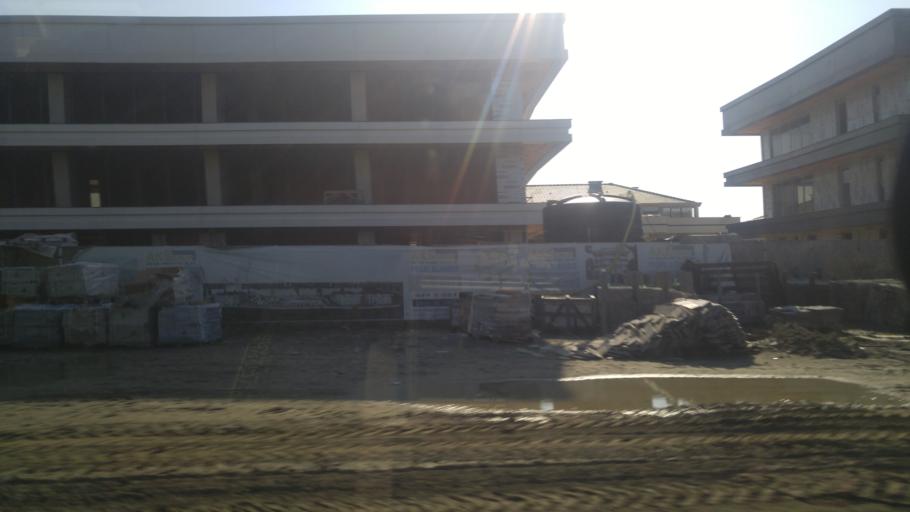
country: TR
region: Istanbul
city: Kumburgaz
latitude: 41.0166
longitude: 28.4867
